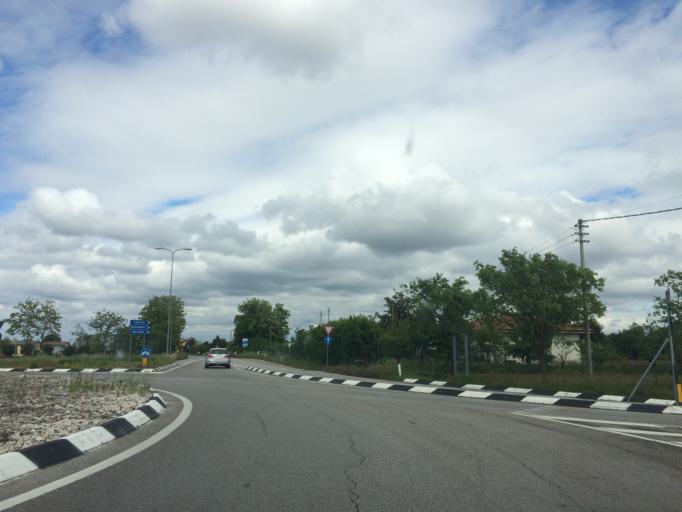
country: IT
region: Veneto
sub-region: Provincia di Padova
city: Cittadella
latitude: 45.6516
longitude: 11.8030
